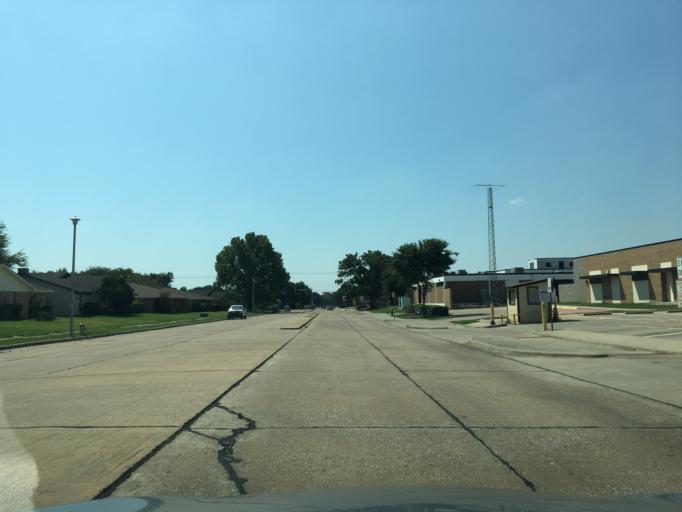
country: US
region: Texas
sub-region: Dallas County
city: Garland
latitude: 32.9325
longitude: -96.6573
